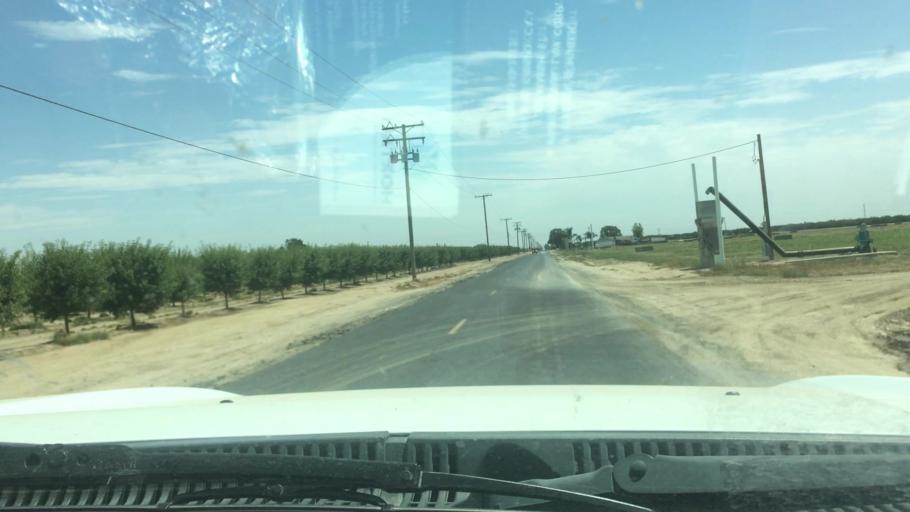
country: US
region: California
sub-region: Tulare County
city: Tipton
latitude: 36.0557
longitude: -119.3220
